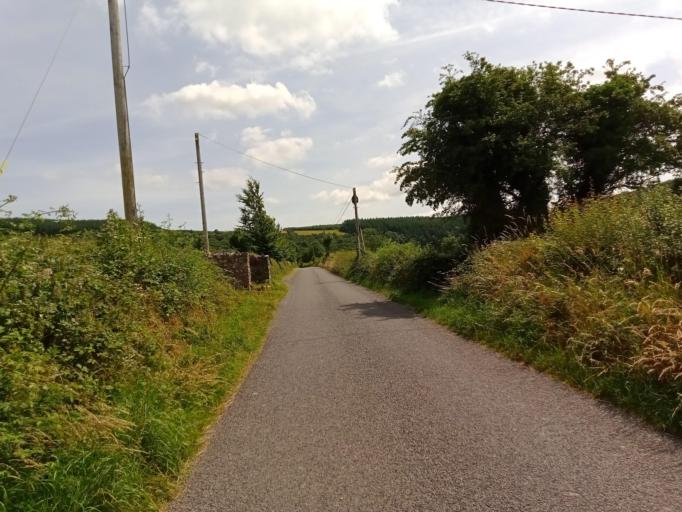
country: IE
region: Leinster
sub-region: Laois
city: Rathdowney
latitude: 52.8076
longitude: -7.4667
